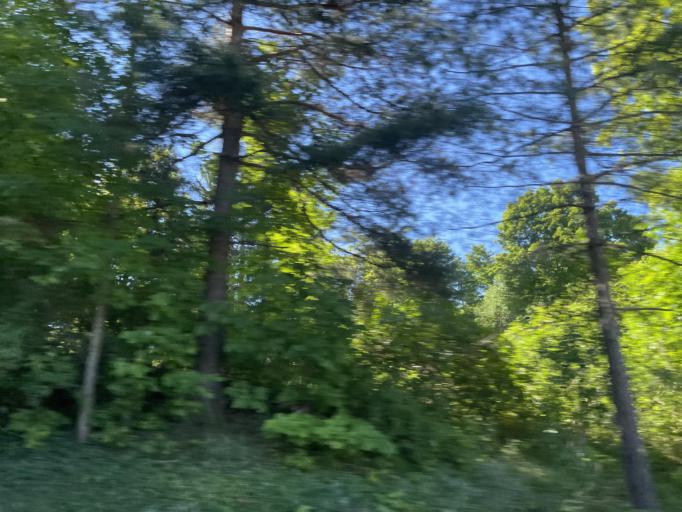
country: US
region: Michigan
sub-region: Benzie County
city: Beulah
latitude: 44.6174
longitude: -86.0788
